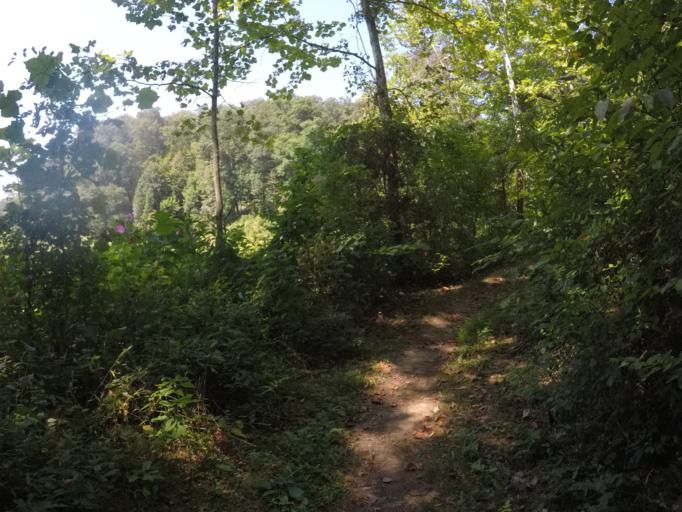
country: US
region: Ohio
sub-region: Lawrence County
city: Ironton
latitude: 38.6242
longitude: -82.6204
